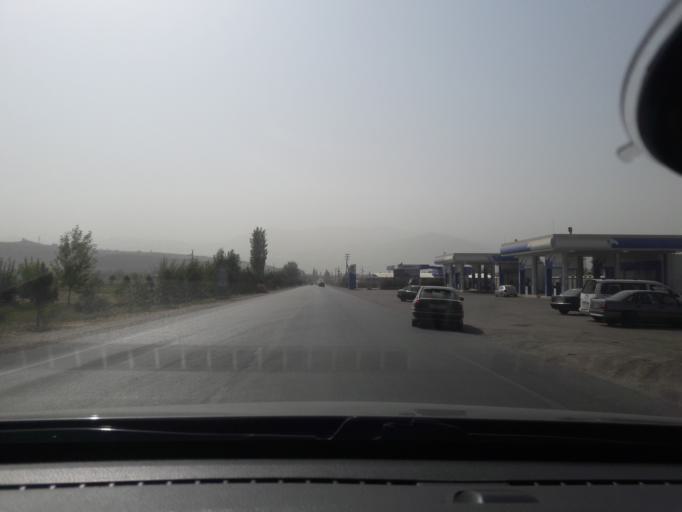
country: TJ
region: Republican Subordination
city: Vahdat
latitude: 38.5323
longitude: 69.0254
